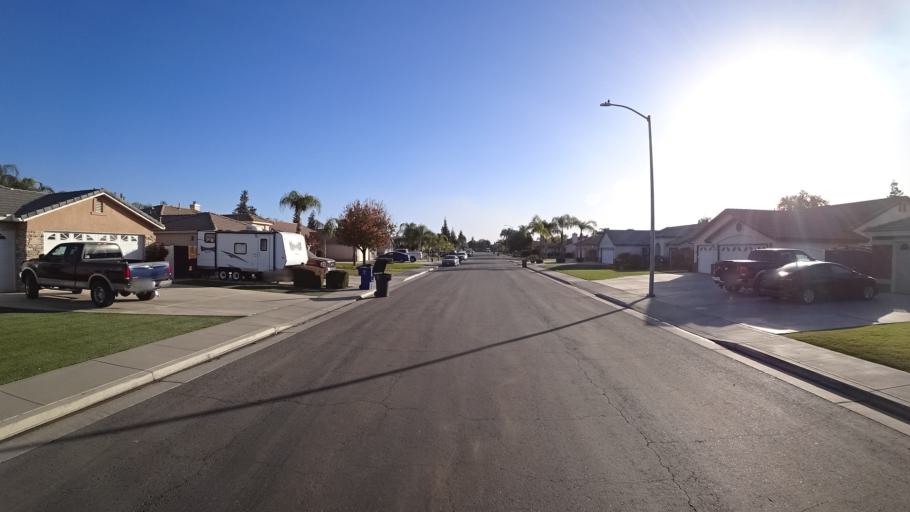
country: US
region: California
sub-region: Kern County
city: Greenfield
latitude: 35.2773
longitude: -119.0378
